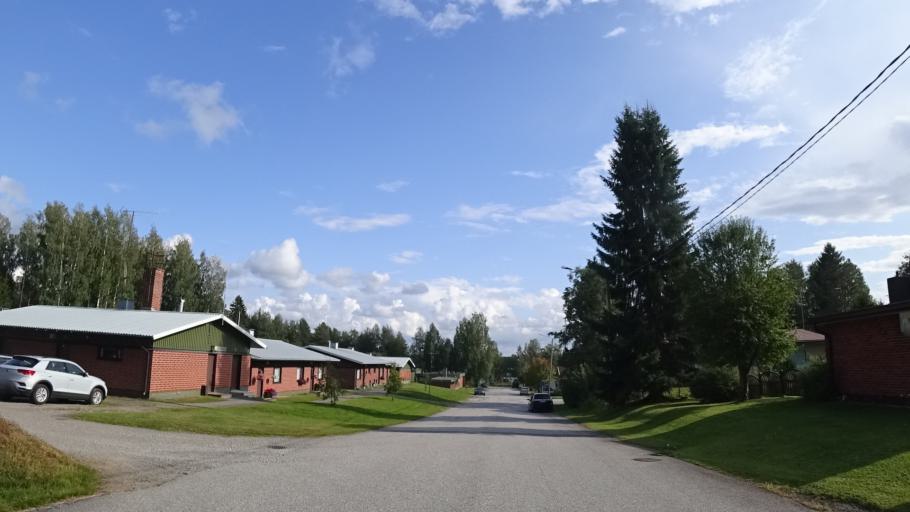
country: FI
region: North Karelia
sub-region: Pielisen Karjala
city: Lieksa
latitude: 63.3342
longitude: 30.0338
